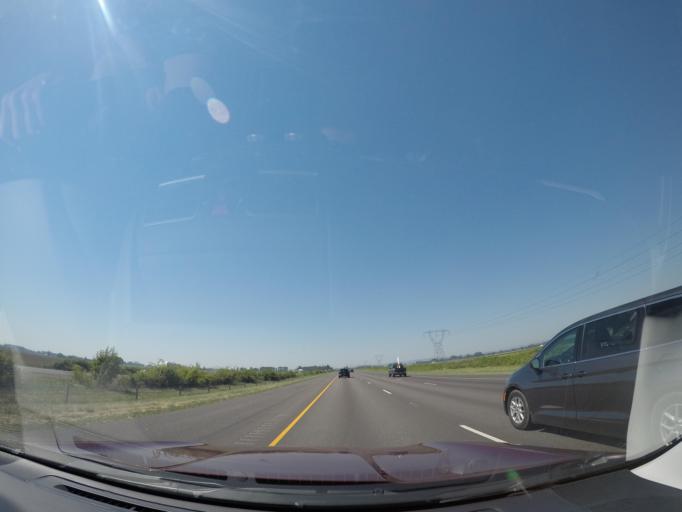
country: US
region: Oregon
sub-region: Marion County
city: Gervais
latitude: 45.0872
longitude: -122.9458
